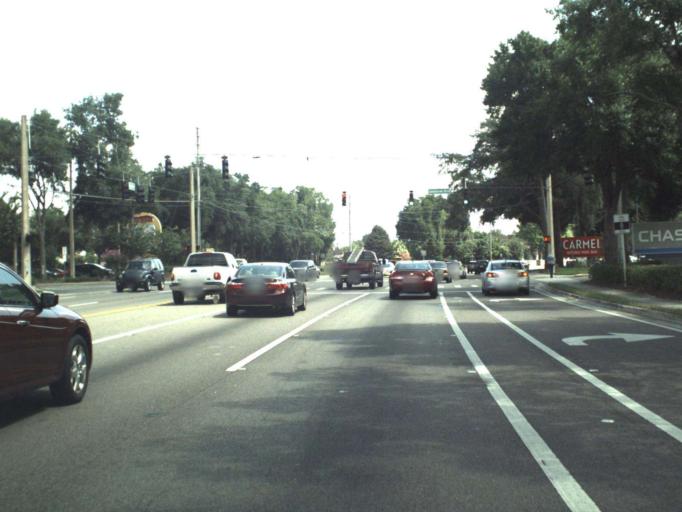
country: US
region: Florida
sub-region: Seminole County
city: Wekiwa Springs
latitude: 28.6822
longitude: -81.4189
